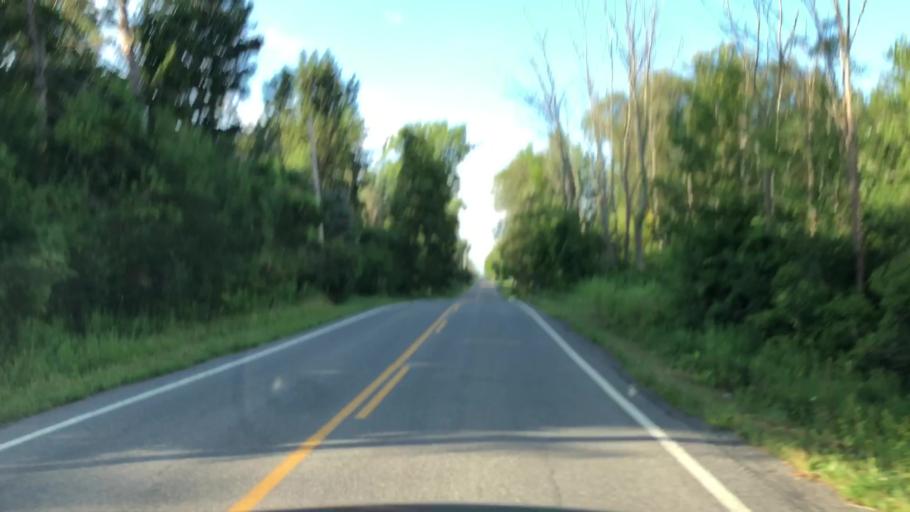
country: US
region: New York
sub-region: Erie County
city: Depew
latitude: 42.8516
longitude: -78.6924
